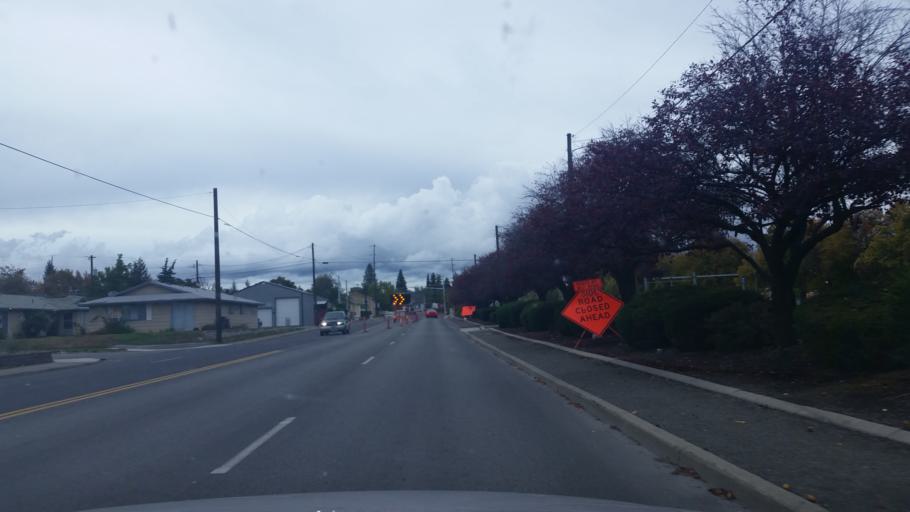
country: US
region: Washington
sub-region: Spokane County
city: Spokane
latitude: 47.6734
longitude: -117.3904
